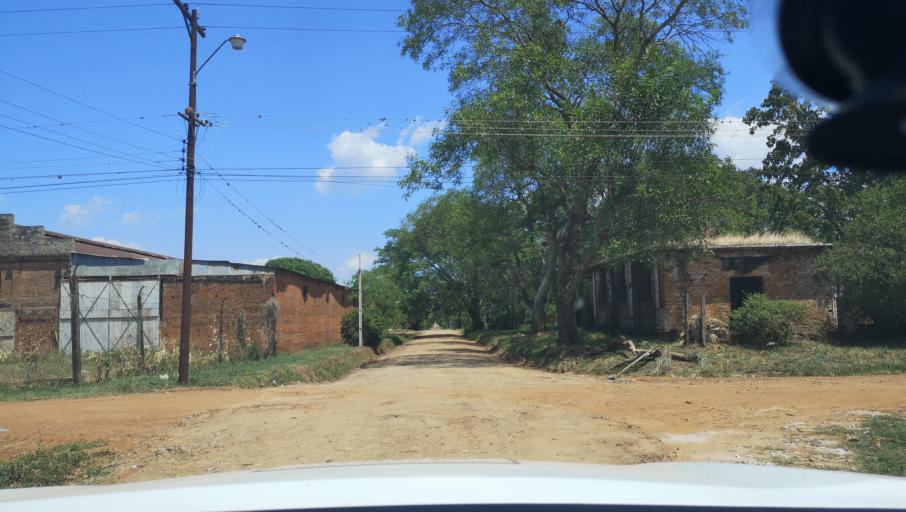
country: PY
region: Itapua
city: Carmen del Parana
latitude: -27.1655
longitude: -56.2384
